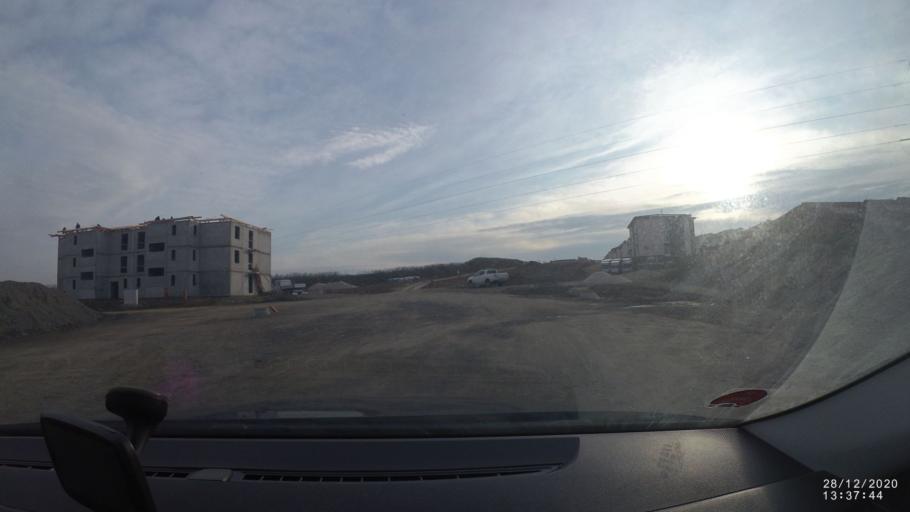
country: CZ
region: Central Bohemia
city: Nehvizdy
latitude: 50.1332
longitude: 14.7428
